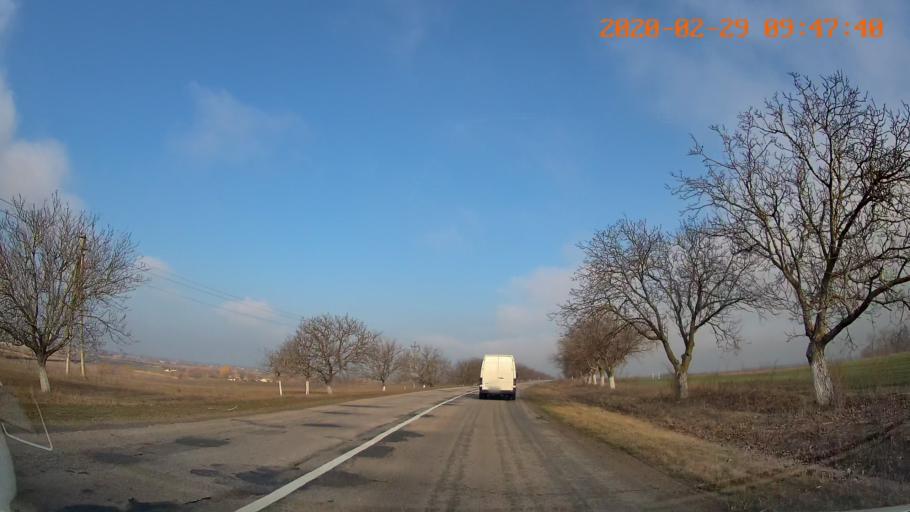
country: MD
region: Telenesti
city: Crasnoe
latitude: 46.6793
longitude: 29.7887
